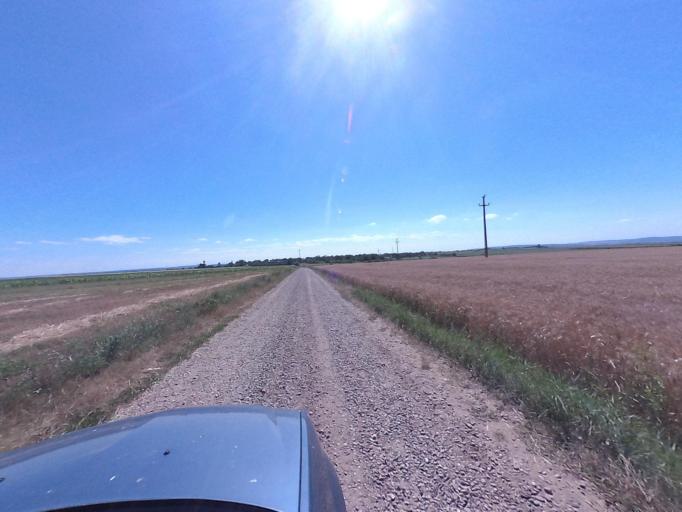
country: RO
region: Vaslui
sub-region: Comuna Costesti
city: Costesti
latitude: 46.4799
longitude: 27.7795
